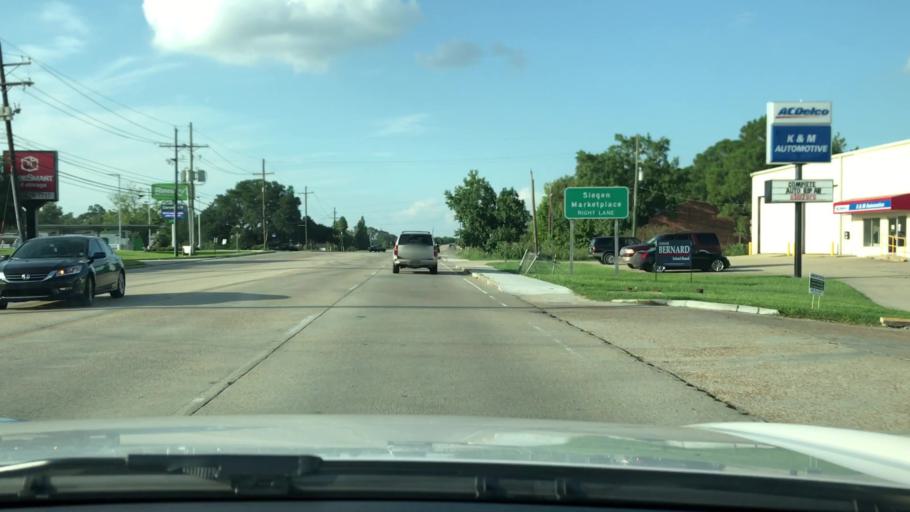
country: US
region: Louisiana
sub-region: East Baton Rouge Parish
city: Village Saint George
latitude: 30.3712
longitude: -91.0727
